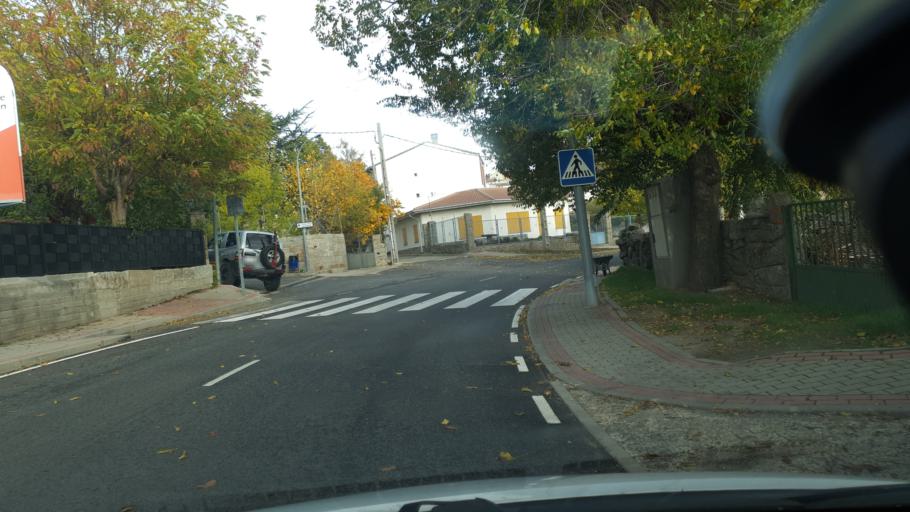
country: ES
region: Castille and Leon
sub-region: Provincia de Avila
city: Navalosa
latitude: 40.4002
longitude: -4.9325
